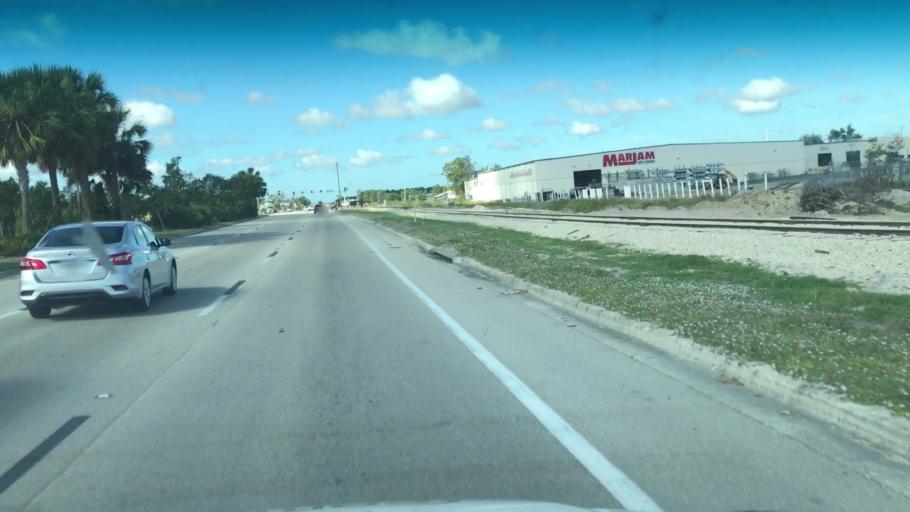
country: US
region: Florida
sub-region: Lee County
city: San Carlos Park
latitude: 26.4928
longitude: -81.8222
